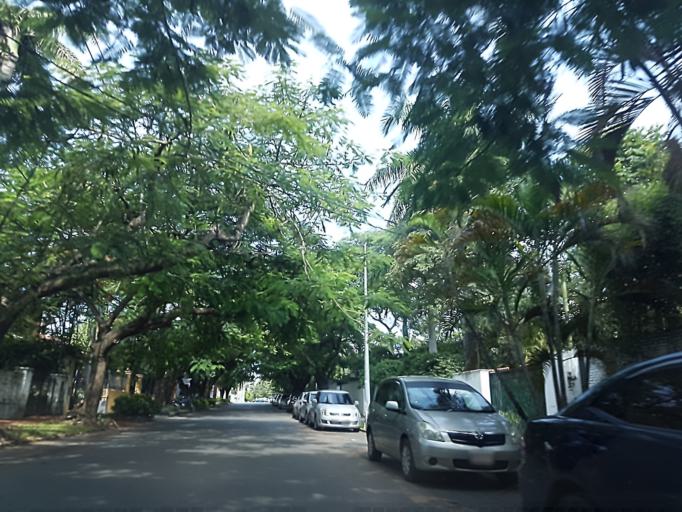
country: PY
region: Asuncion
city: Asuncion
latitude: -25.2829
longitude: -57.5731
